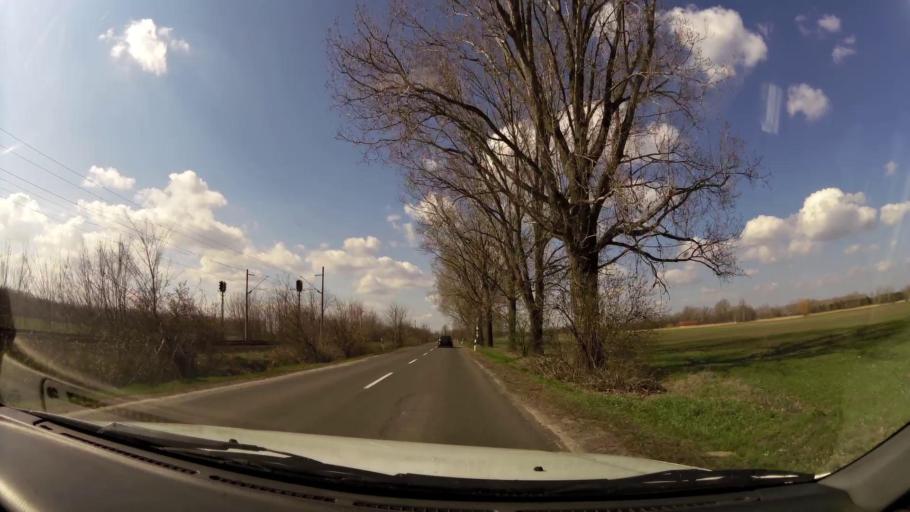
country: HU
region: Pest
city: Nagykata
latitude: 47.3873
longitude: 19.7757
